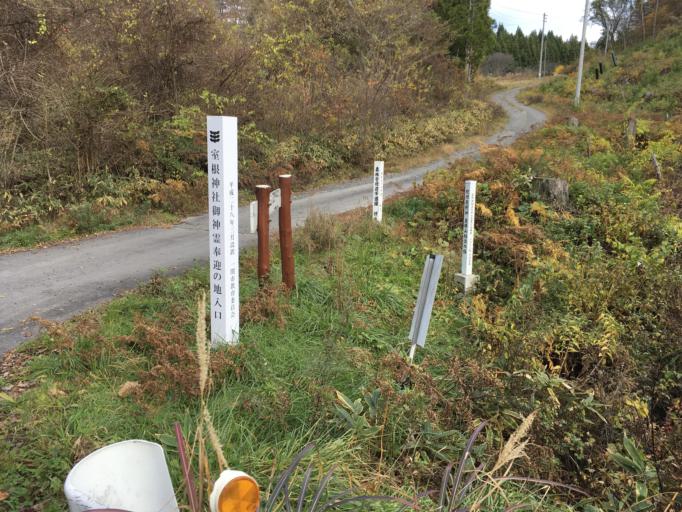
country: JP
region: Iwate
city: Ofunato
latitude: 38.8864
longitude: 141.4628
